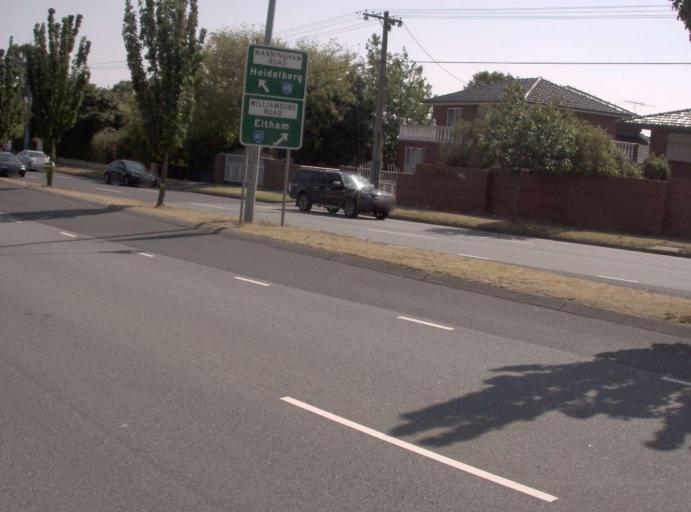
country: AU
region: Victoria
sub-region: Manningham
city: Doncaster
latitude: -37.7814
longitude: 145.1236
